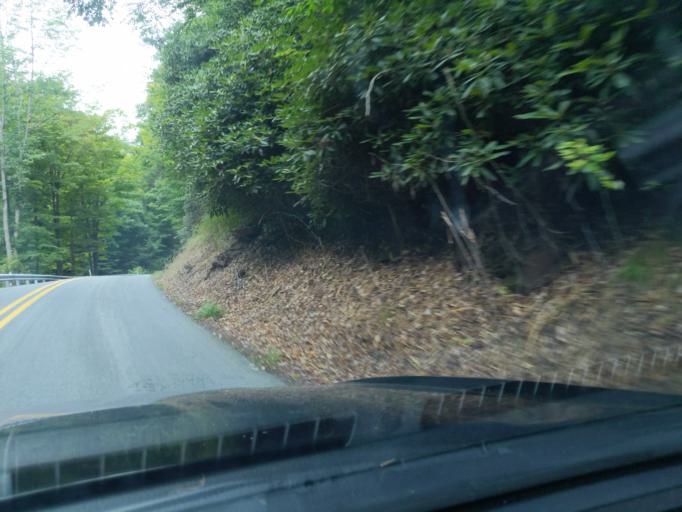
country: US
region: Pennsylvania
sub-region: Cambria County
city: Portage
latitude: 40.3357
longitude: -78.5819
